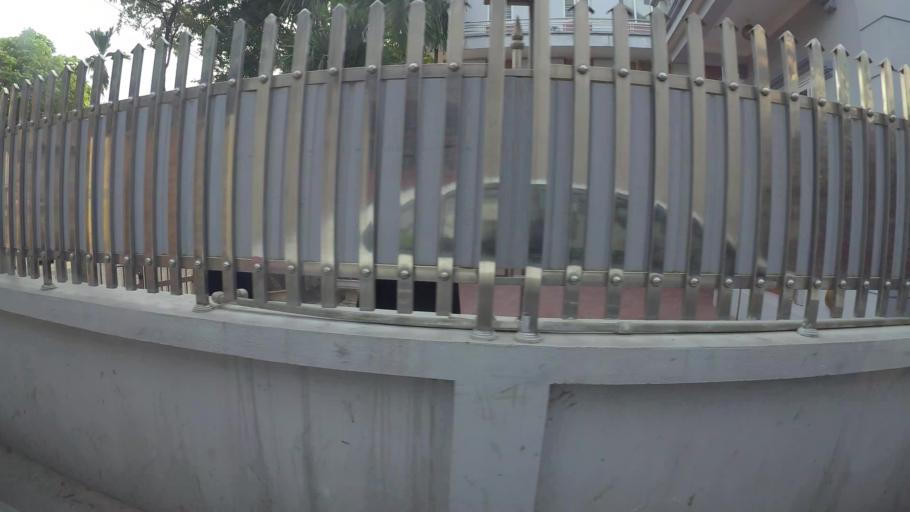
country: VN
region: Ha Noi
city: Ha Dong
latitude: 20.9944
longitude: 105.7531
